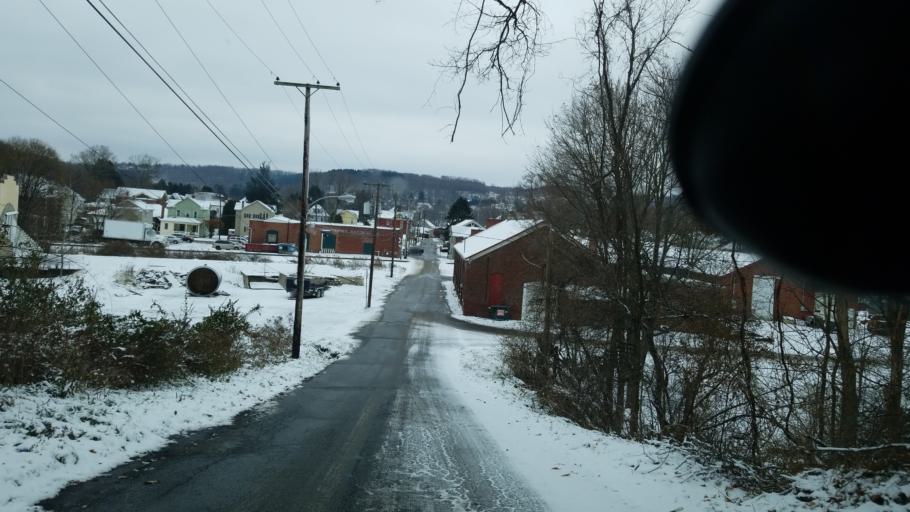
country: US
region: Pennsylvania
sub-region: Jefferson County
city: Punxsutawney
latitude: 40.9453
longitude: -78.9769
